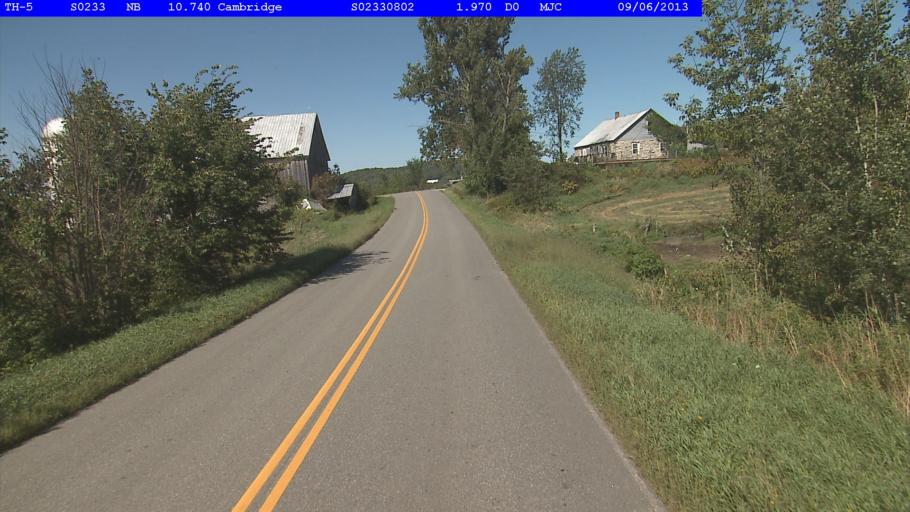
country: US
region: Vermont
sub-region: Chittenden County
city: Jericho
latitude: 44.6102
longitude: -72.8564
